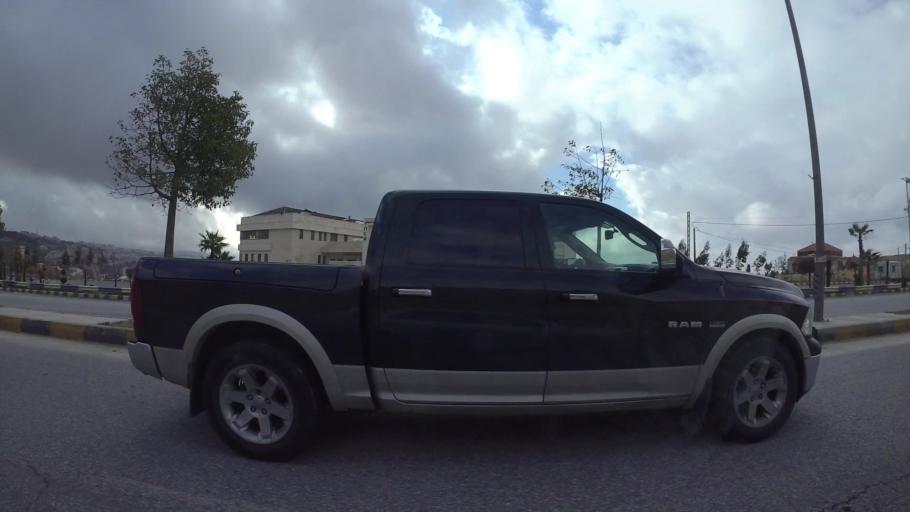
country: JO
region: Amman
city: Al Jubayhah
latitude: 32.0513
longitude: 35.8712
